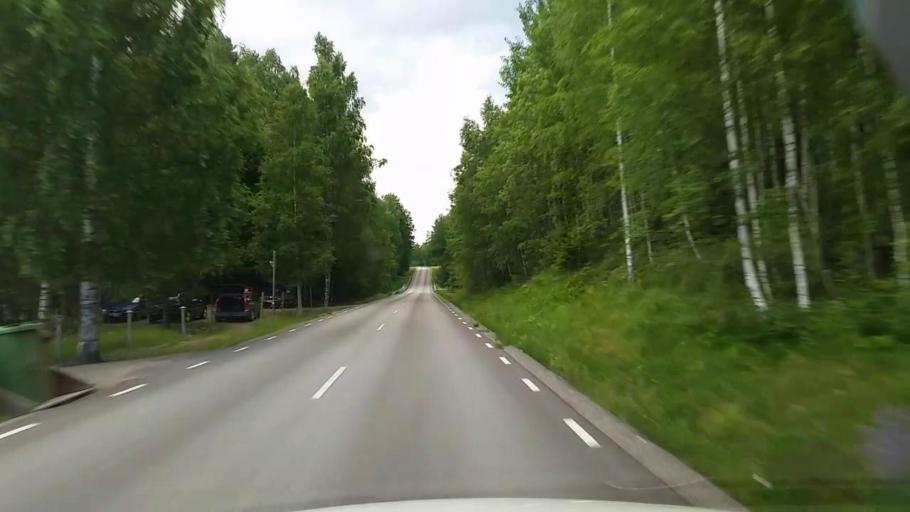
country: SE
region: Vaestmanland
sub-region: Skinnskattebergs Kommun
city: Skinnskatteberg
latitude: 59.7678
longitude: 15.8499
